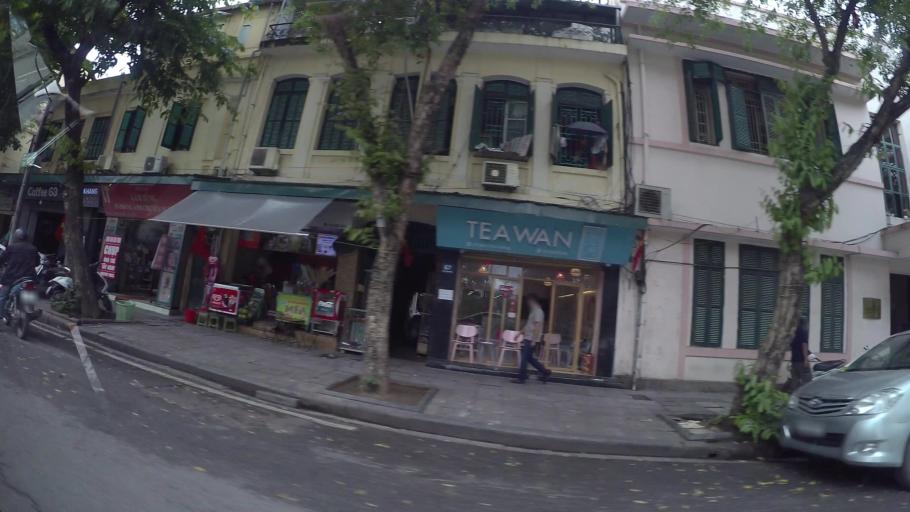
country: VN
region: Ha Noi
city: Hoan Kiem
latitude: 21.0301
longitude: 105.8540
